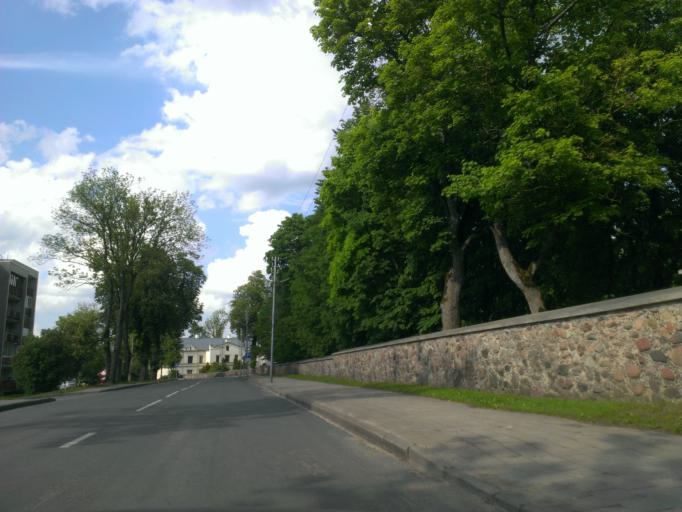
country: LT
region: Klaipedos apskritis
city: Kretinga
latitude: 55.8984
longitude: 21.2471
